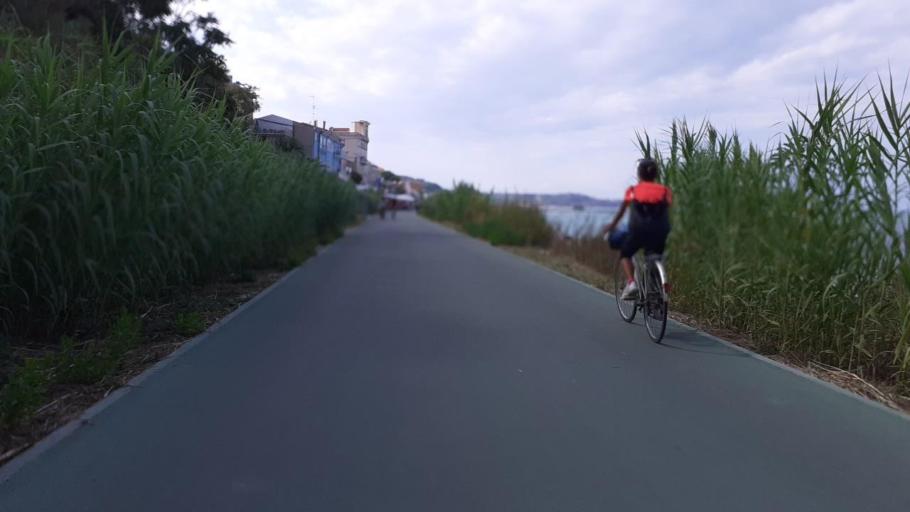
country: IT
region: Abruzzo
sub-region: Provincia di Chieti
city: Marina di San Vito
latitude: 42.3033
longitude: 14.4537
